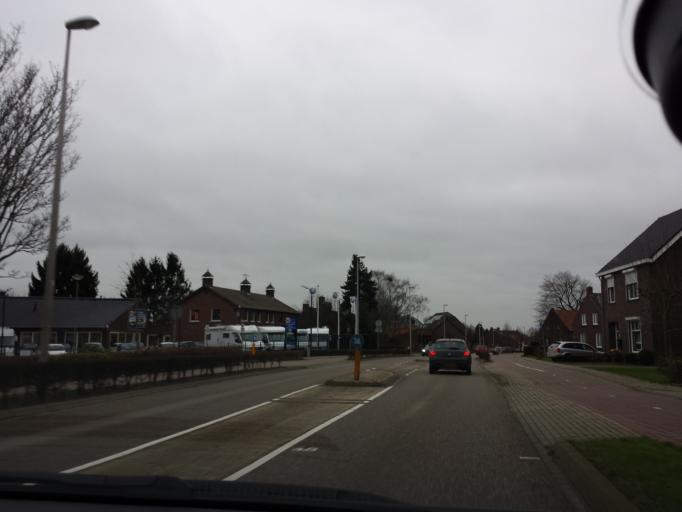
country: NL
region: Limburg
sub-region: Gemeente Roerdalen
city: Melick
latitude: 51.1581
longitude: 6.0080
